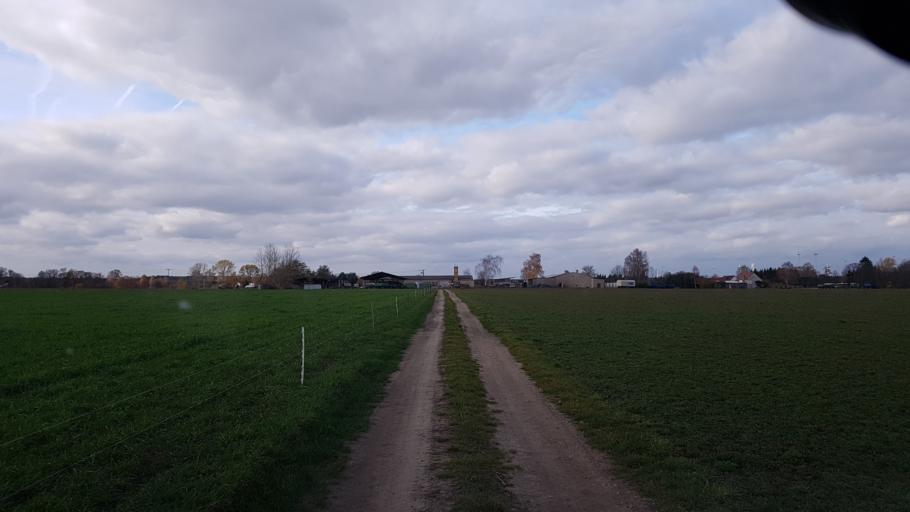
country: DE
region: Brandenburg
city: Sallgast
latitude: 51.6030
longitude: 13.8675
